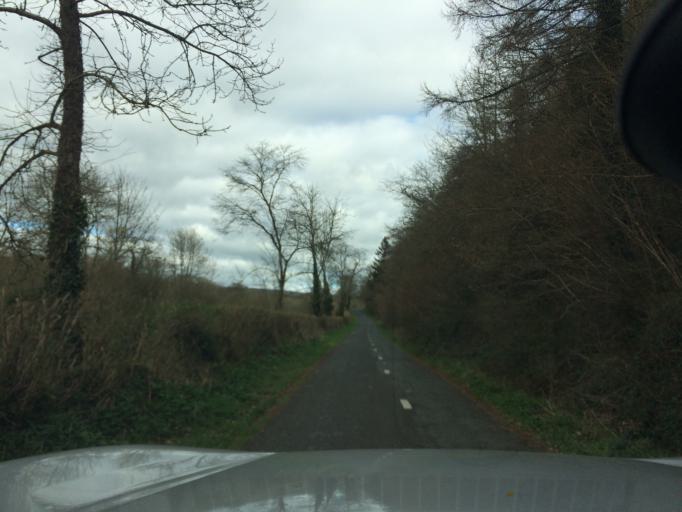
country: IE
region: Munster
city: Carrick-on-Suir
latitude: 52.2847
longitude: -7.4050
